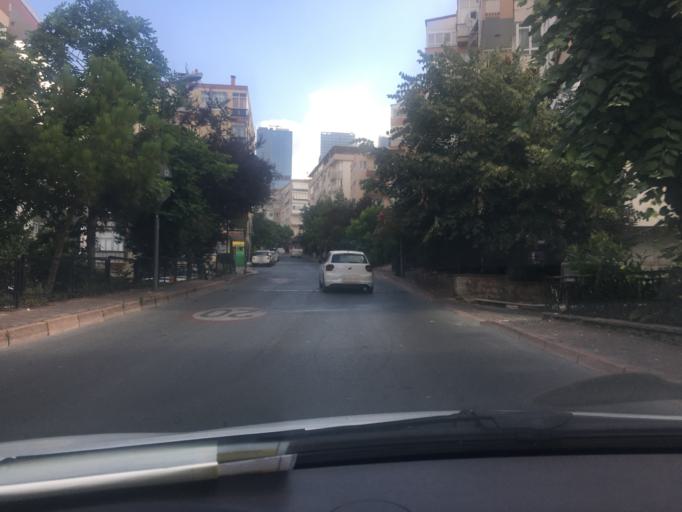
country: TR
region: Istanbul
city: Sisli
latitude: 41.0589
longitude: 28.9988
